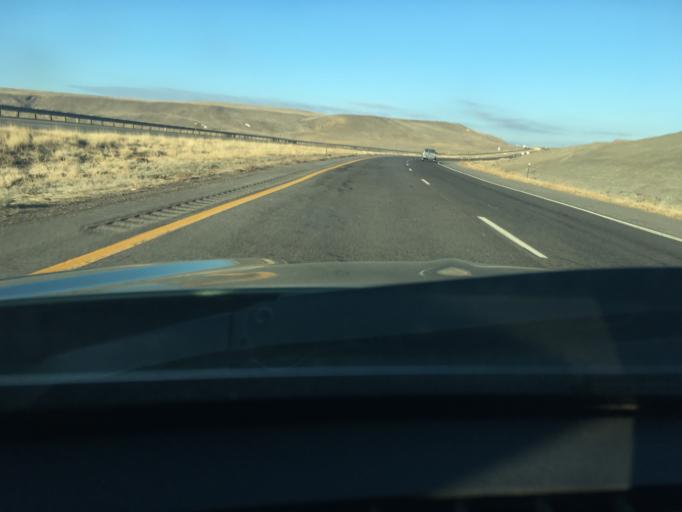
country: US
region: Colorado
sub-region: Delta County
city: Delta
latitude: 38.7508
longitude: -108.1621
